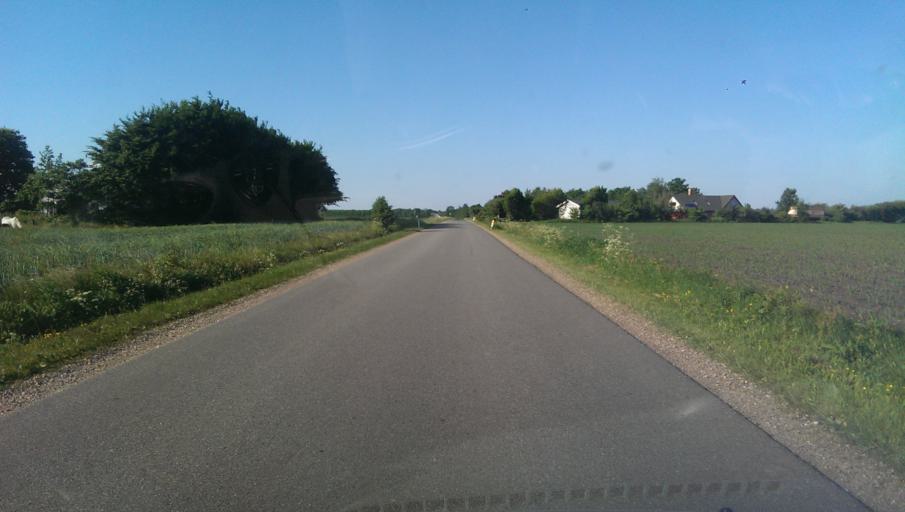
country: DK
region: South Denmark
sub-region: Esbjerg Kommune
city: Bramming
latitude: 55.5366
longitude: 8.6956
